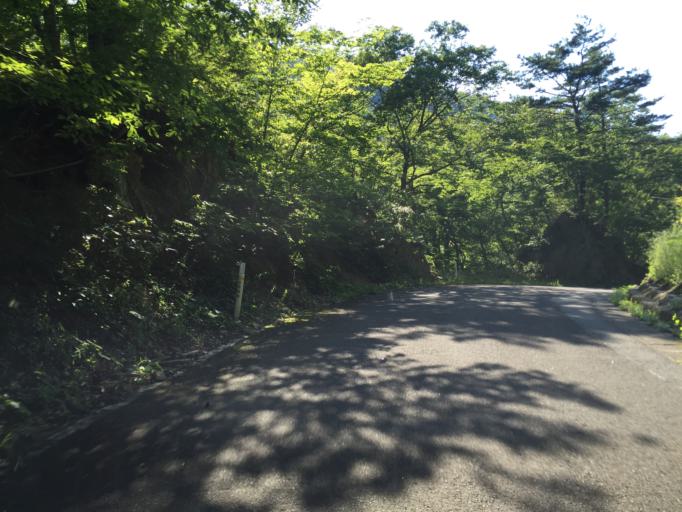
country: JP
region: Yamagata
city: Takahata
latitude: 37.9622
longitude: 140.3450
